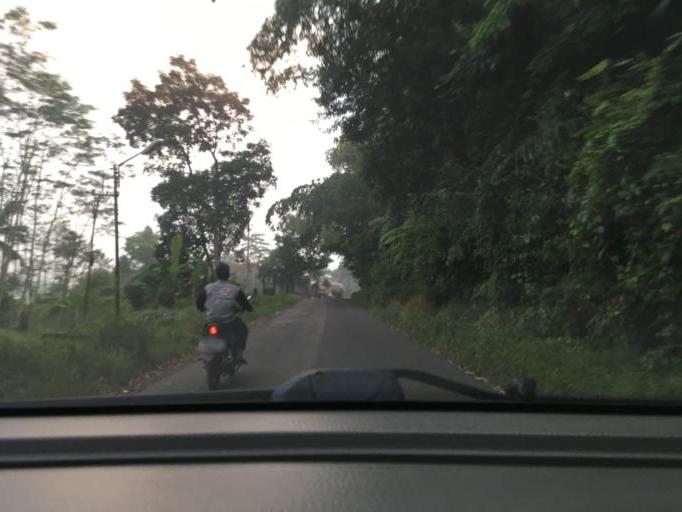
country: ID
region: West Java
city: Kampungdesa Pamokolan
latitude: -7.1933
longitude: 108.1985
